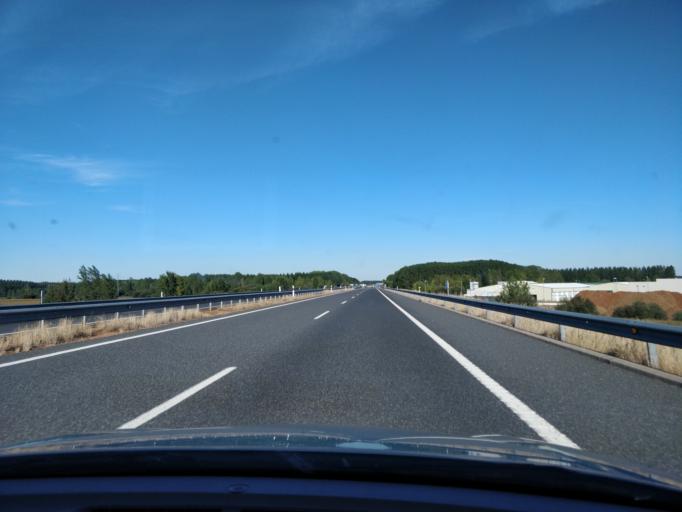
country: ES
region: Castille and Leon
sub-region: Provincia de Leon
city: Villarejo de Orbigo
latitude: 42.4484
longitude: -5.9179
